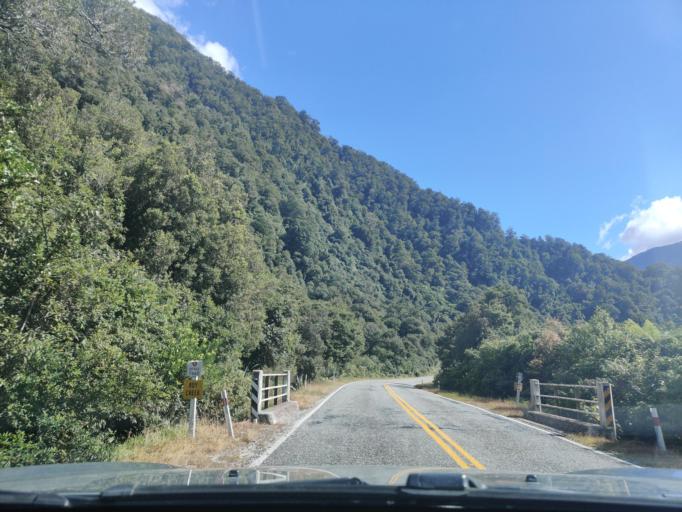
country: NZ
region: Otago
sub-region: Queenstown-Lakes District
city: Wanaka
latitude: -43.9520
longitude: 169.1482
